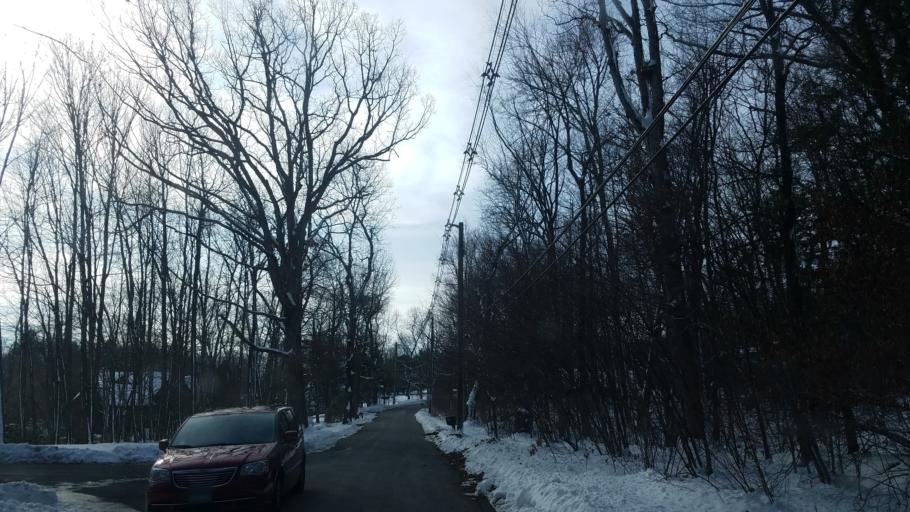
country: US
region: Connecticut
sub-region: Hartford County
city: Canton Valley
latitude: 41.8444
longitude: -72.9076
